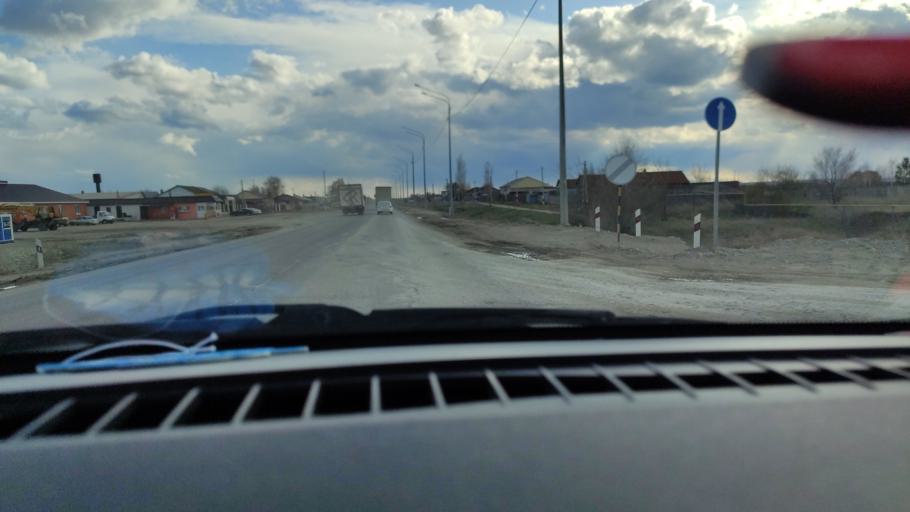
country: RU
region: Saratov
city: Sinodskoye
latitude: 51.9940
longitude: 46.6715
